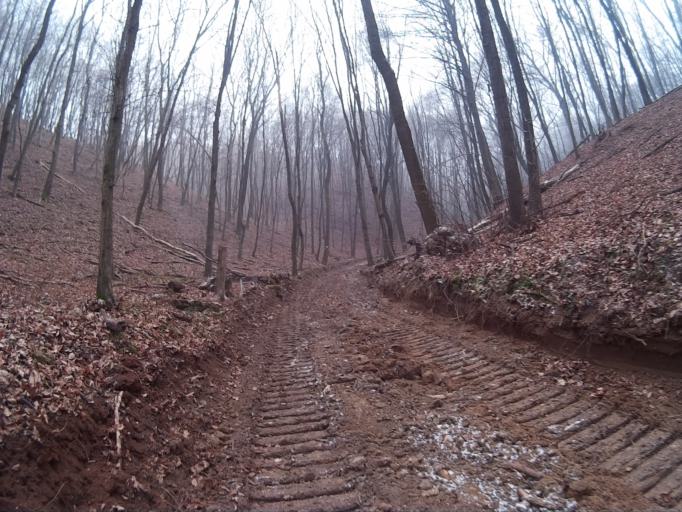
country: HU
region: Komarom-Esztergom
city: Oroszlany
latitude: 47.4542
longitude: 18.3959
